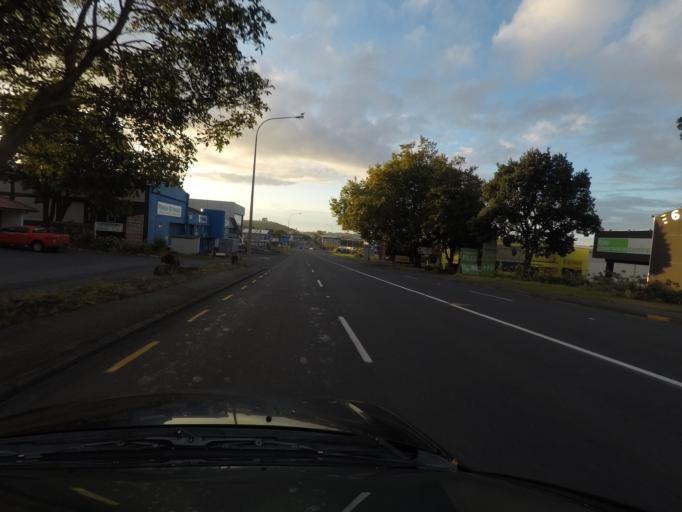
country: NZ
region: Auckland
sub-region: Auckland
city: Tamaki
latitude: -36.9153
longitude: 174.8224
